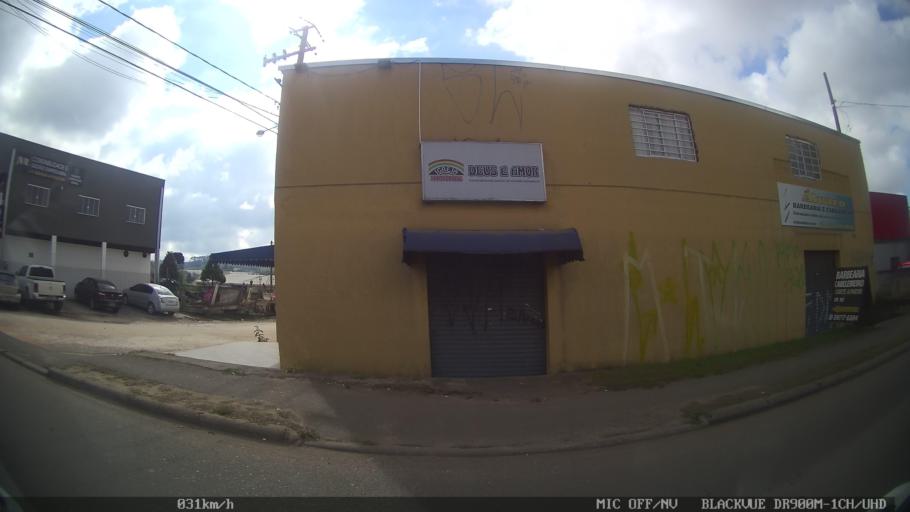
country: BR
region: Parana
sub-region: Colombo
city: Colombo
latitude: -25.3466
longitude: -49.1824
